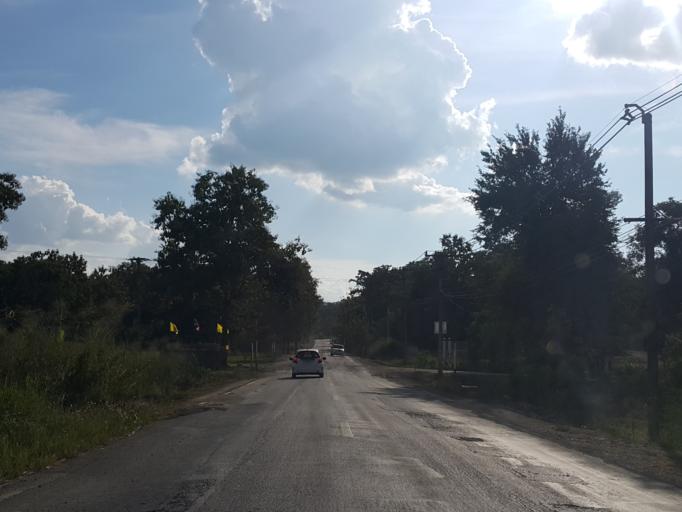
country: TH
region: Chiang Mai
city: Mae On
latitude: 18.8134
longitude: 99.2528
